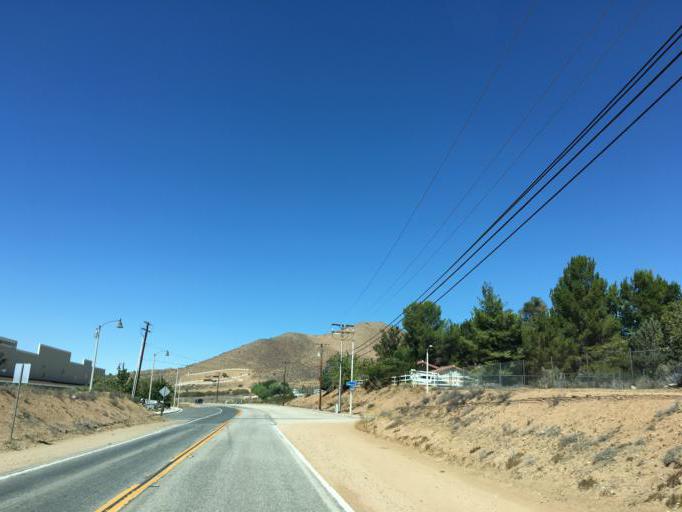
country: US
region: California
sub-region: Los Angeles County
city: Acton
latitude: 34.4810
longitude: -118.1621
